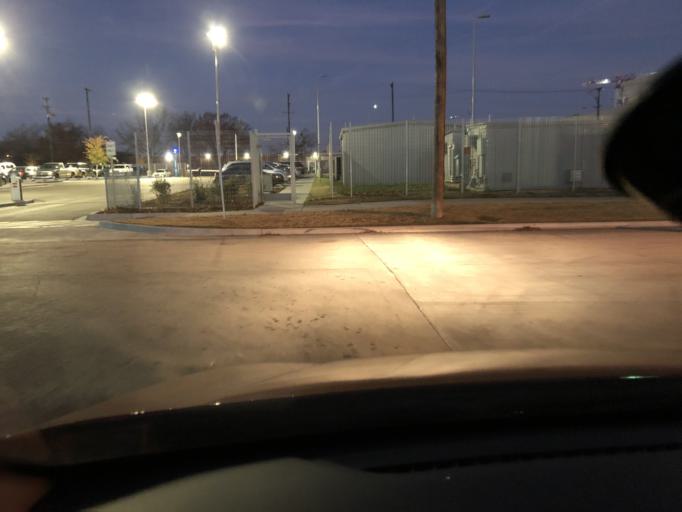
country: US
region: Texas
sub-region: Dallas County
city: Dallas
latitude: 32.8143
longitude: -96.8365
